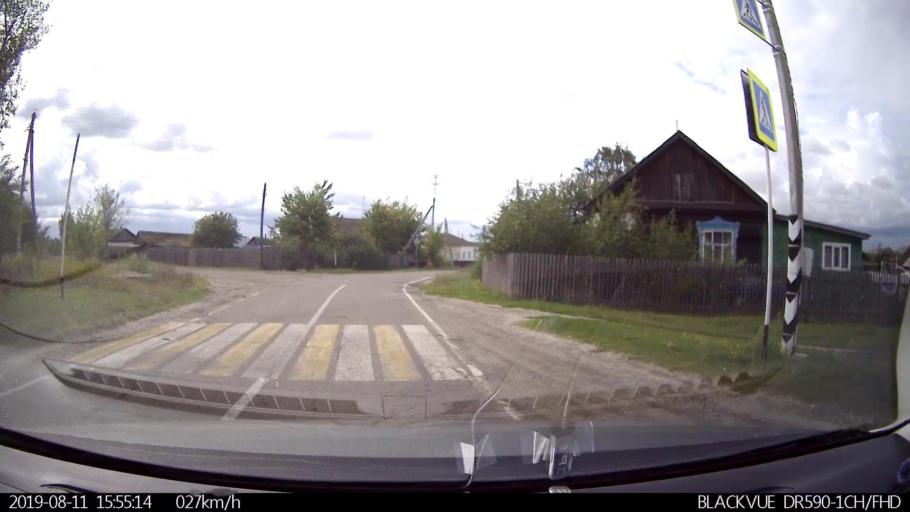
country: RU
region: Ulyanovsk
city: Ignatovka
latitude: 53.9447
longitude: 47.6553
